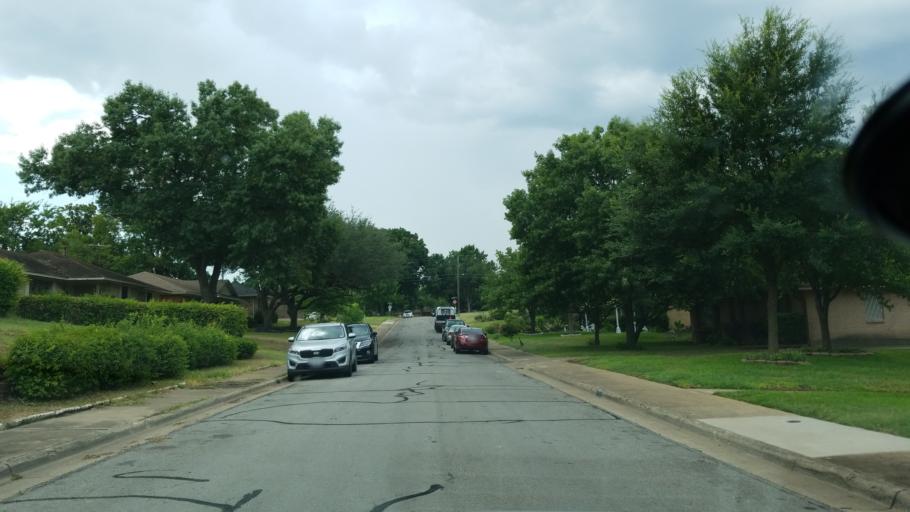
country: US
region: Texas
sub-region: Dallas County
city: Duncanville
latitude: 32.6688
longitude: -96.8394
